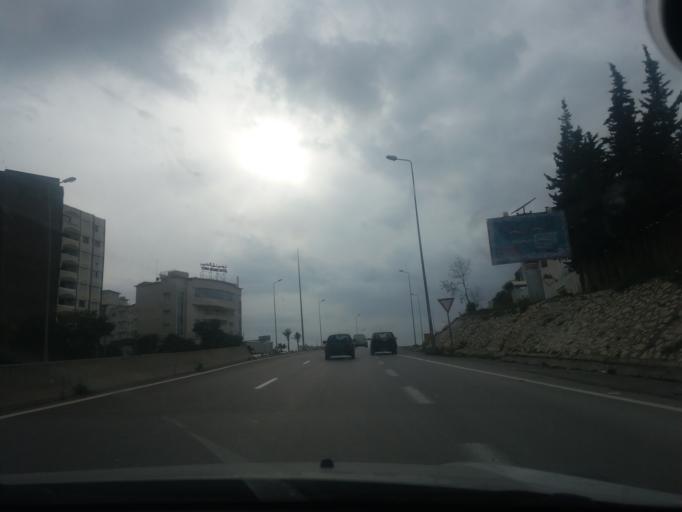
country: TN
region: Ariana
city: Ariana
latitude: 36.8563
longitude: 10.1635
